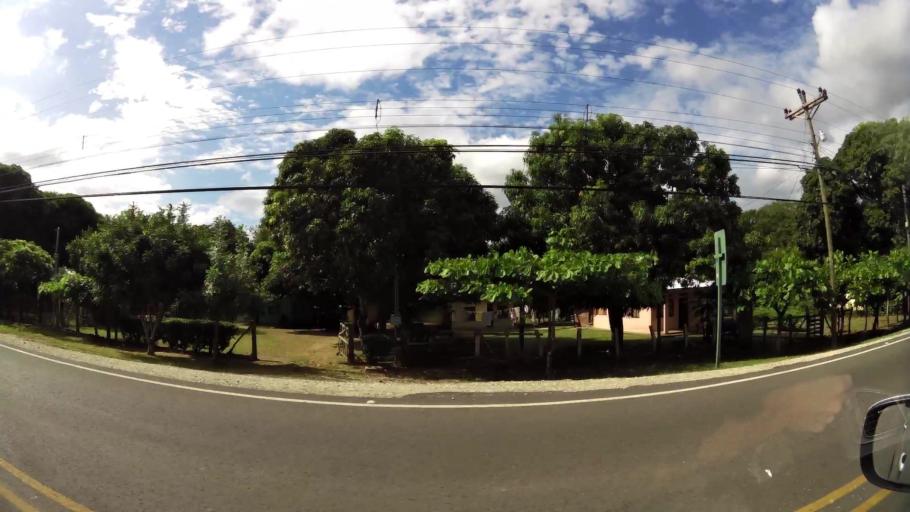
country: CR
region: Guanacaste
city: Hojancha
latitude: 10.1128
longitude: -85.3460
